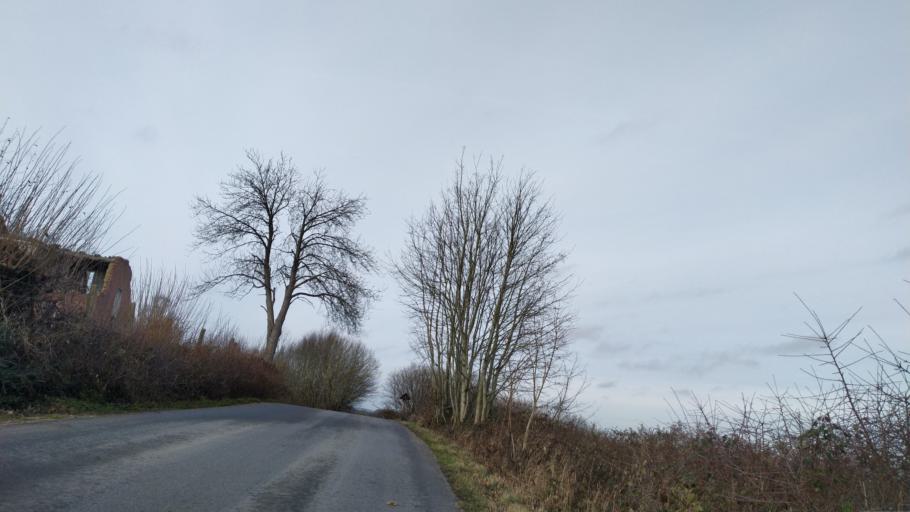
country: DE
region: Schleswig-Holstein
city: Malente
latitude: 54.1958
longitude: 10.6062
